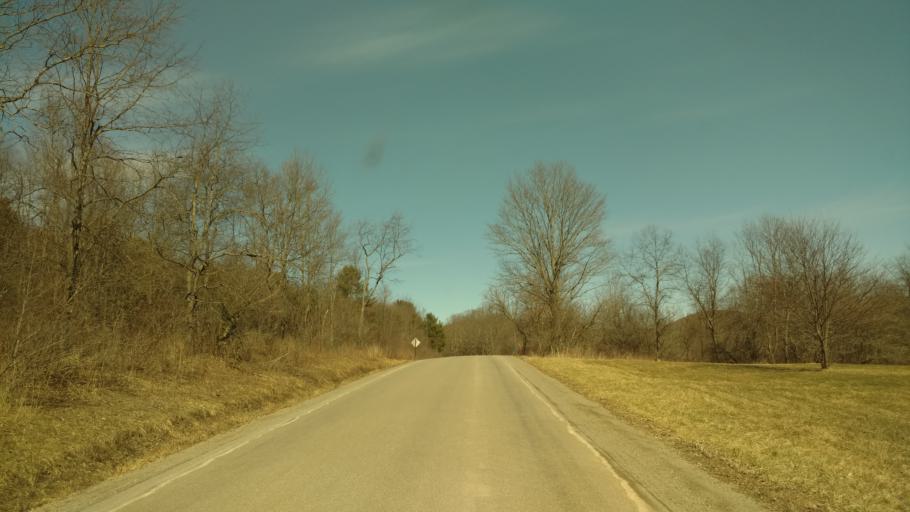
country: US
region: New York
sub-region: Allegany County
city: Wellsville
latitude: 42.0494
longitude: -77.9319
